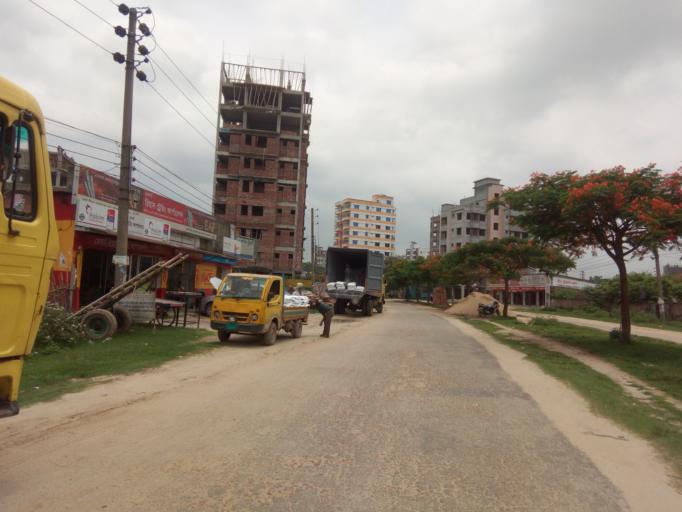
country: BD
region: Dhaka
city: Paltan
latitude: 23.7640
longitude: 90.4339
